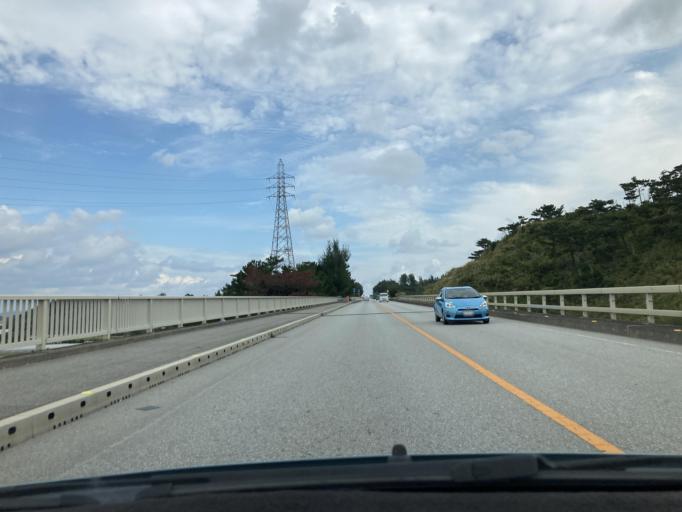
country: JP
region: Okinawa
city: Ishikawa
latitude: 26.4934
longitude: 127.8557
